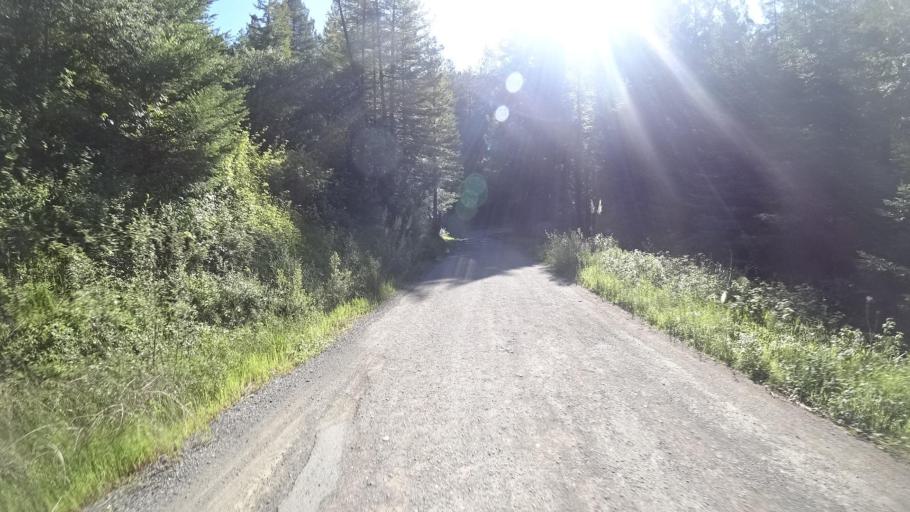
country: US
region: California
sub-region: Humboldt County
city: Rio Dell
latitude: 40.4603
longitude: -123.9957
